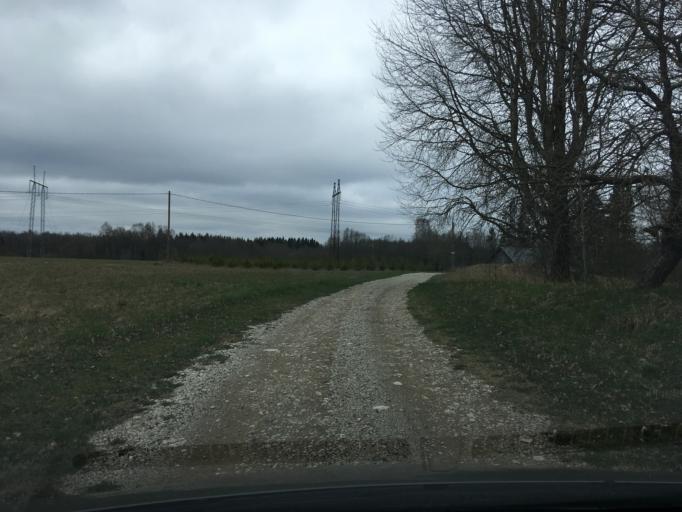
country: EE
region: Harju
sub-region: Raasiku vald
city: Arukula
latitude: 59.2743
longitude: 25.1127
